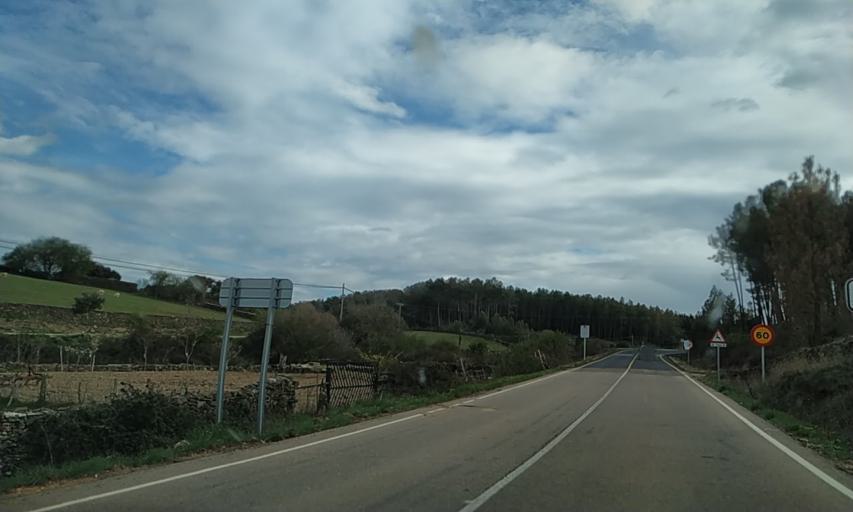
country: ES
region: Castille and Leon
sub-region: Provincia de Salamanca
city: Robleda
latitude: 40.3821
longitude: -6.6109
